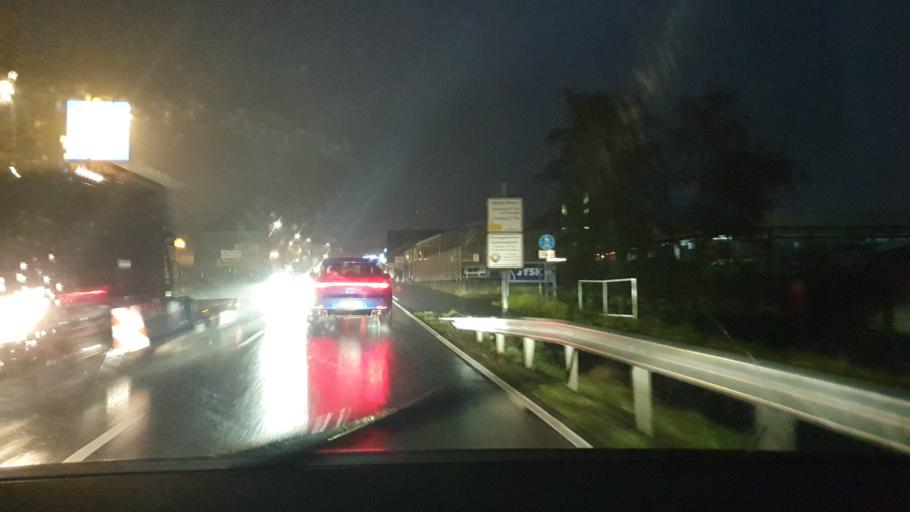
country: DE
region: Rheinland-Pfalz
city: Rennerod
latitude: 50.6008
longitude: 8.0637
